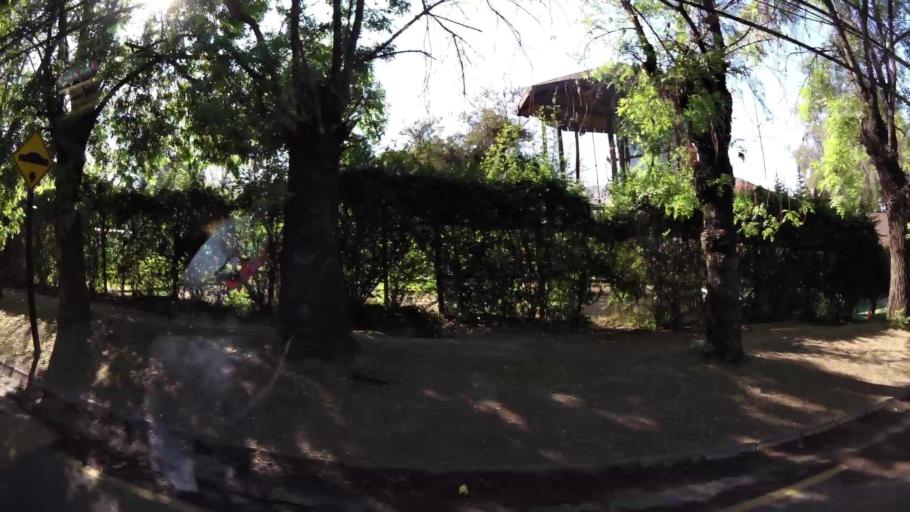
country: CL
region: Santiago Metropolitan
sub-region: Provincia de Chacabuco
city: Chicureo Abajo
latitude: -33.3397
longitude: -70.6679
